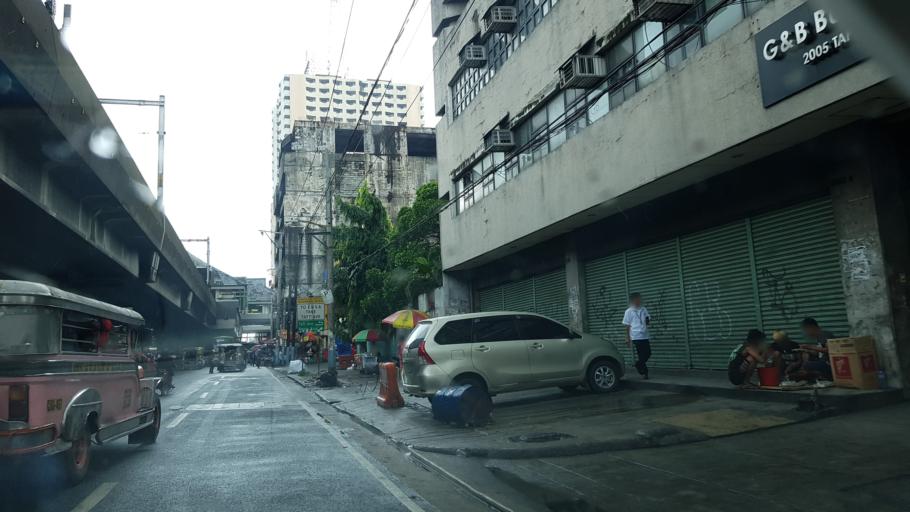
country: PH
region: Metro Manila
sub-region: Makati City
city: Makati City
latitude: 14.5559
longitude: 120.9967
